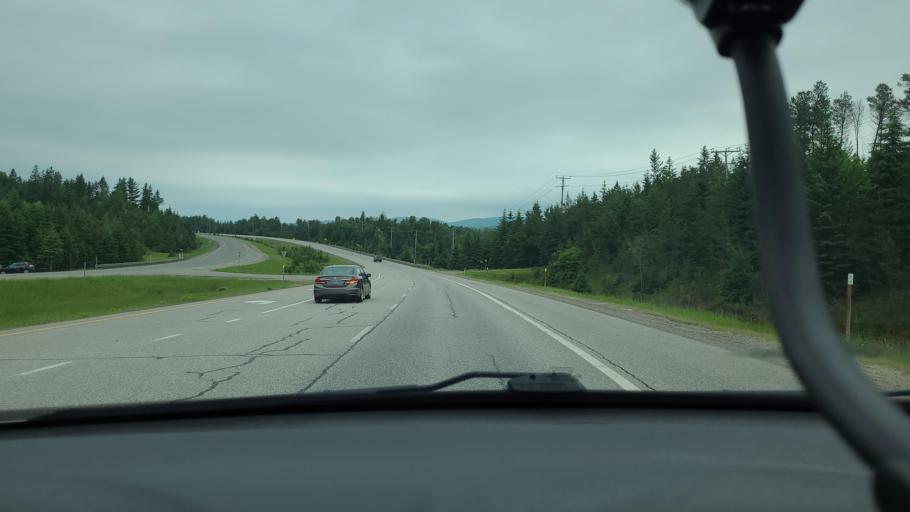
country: CA
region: Quebec
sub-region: Laurentides
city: Labelle
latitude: 46.2397
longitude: -74.7137
